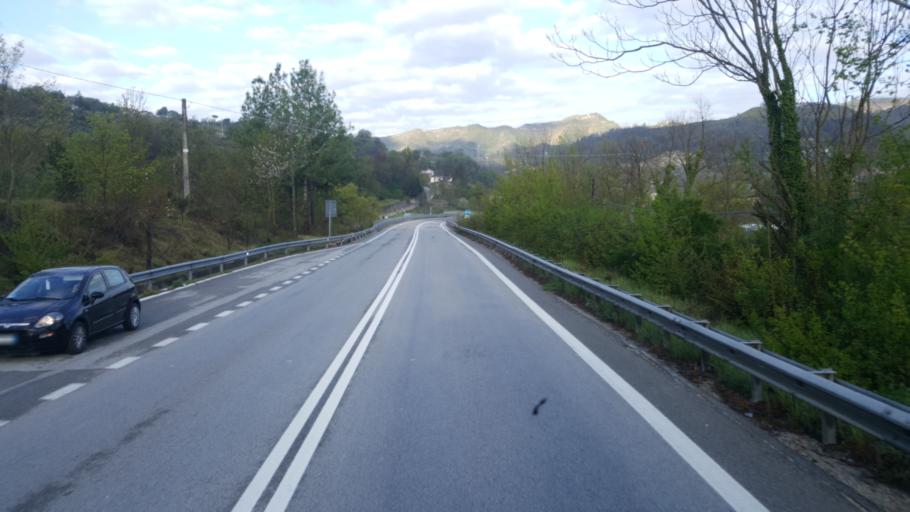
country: IT
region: The Marches
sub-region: Provincia di Ascoli Piceno
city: Ascoli Piceno
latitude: 42.8489
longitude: 13.5469
